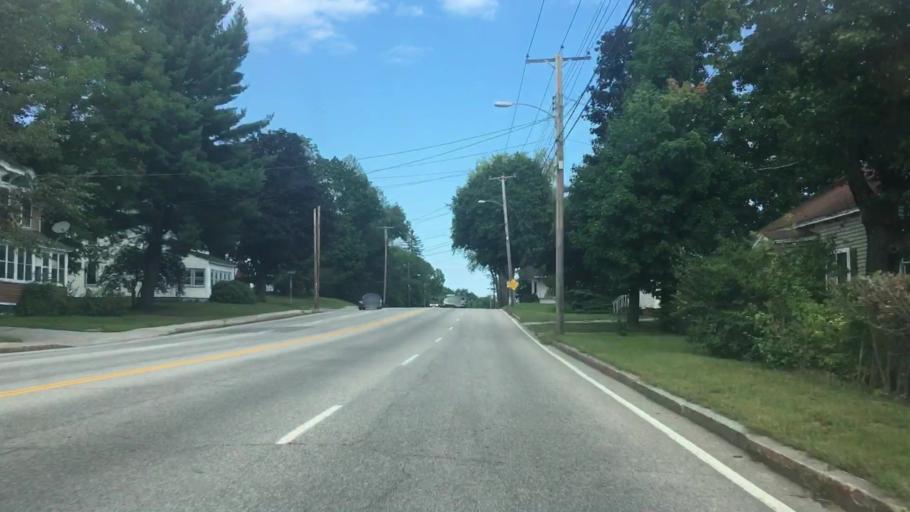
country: US
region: Maine
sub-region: Androscoggin County
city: Auburn
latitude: 44.0855
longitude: -70.2399
